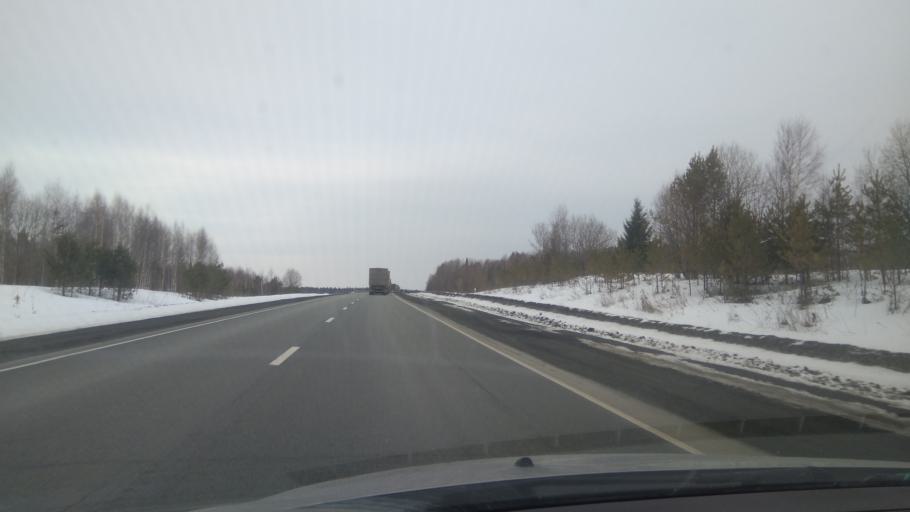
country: RU
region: Sverdlovsk
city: Bisert'
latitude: 56.8164
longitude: 58.7495
